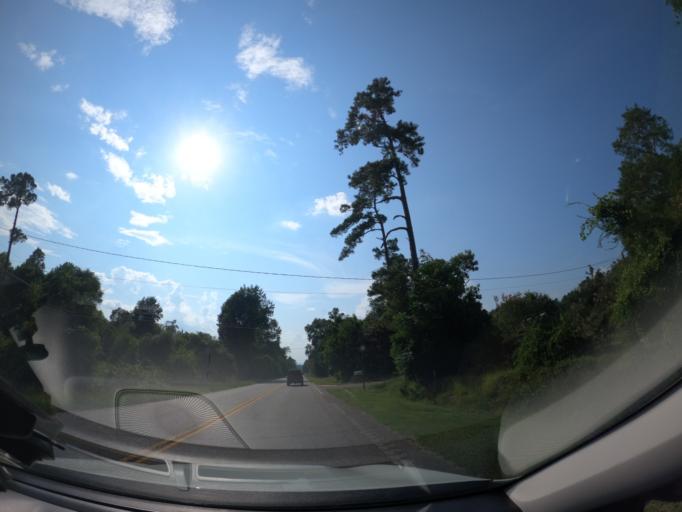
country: US
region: South Carolina
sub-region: Aiken County
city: Clearwater
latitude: 33.4232
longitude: -81.8614
